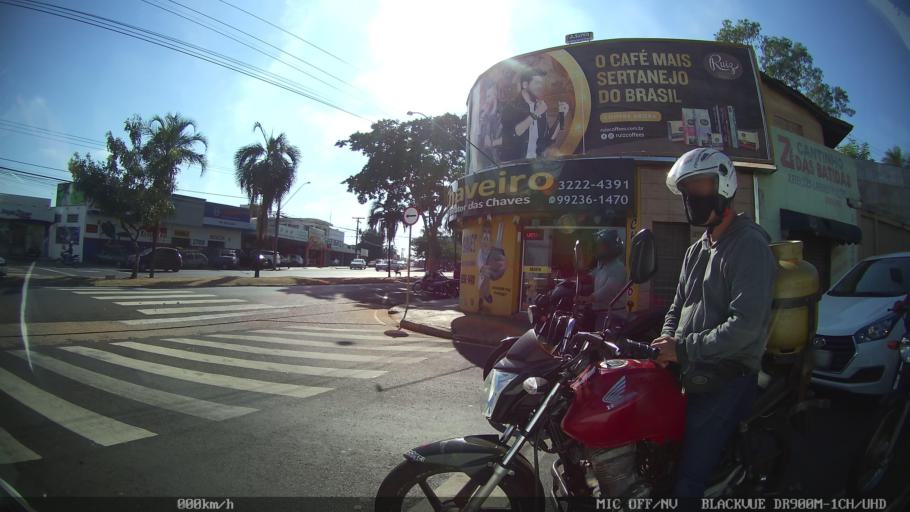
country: BR
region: Sao Paulo
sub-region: Sao Jose Do Rio Preto
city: Sao Jose do Rio Preto
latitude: -20.8096
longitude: -49.3990
